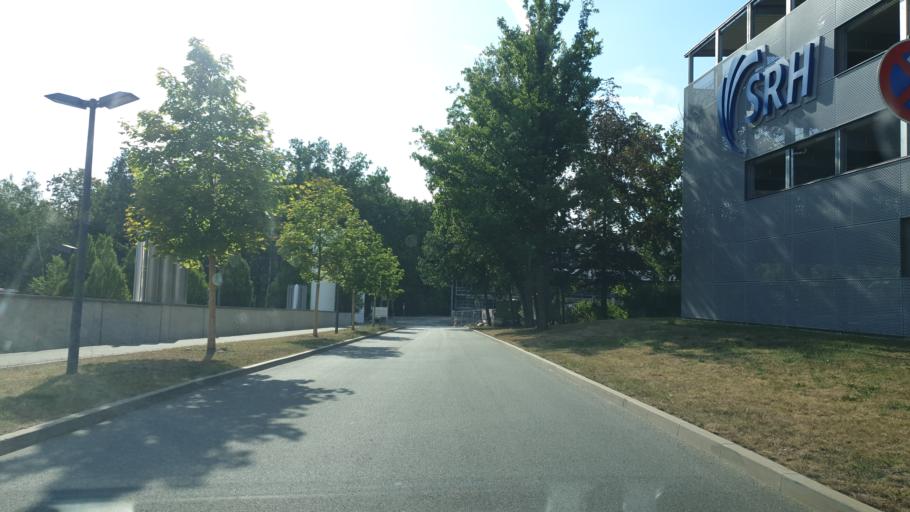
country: DE
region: Thuringia
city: Gera
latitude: 50.8690
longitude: 12.0500
